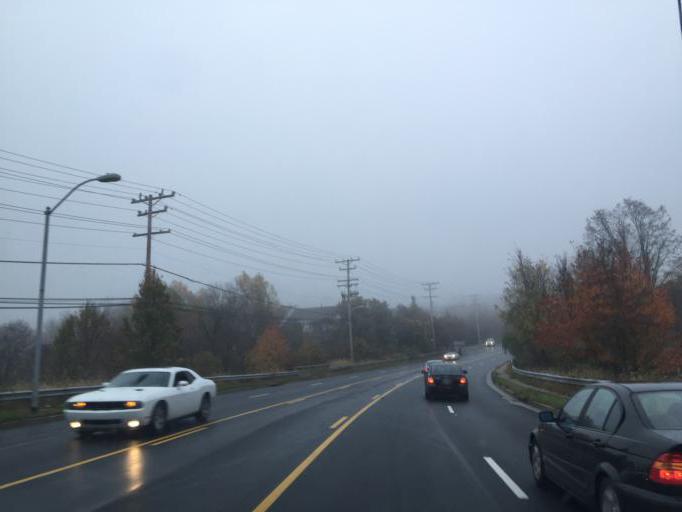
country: US
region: Maryland
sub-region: Baltimore County
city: Randallstown
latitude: 39.3887
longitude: -76.7868
